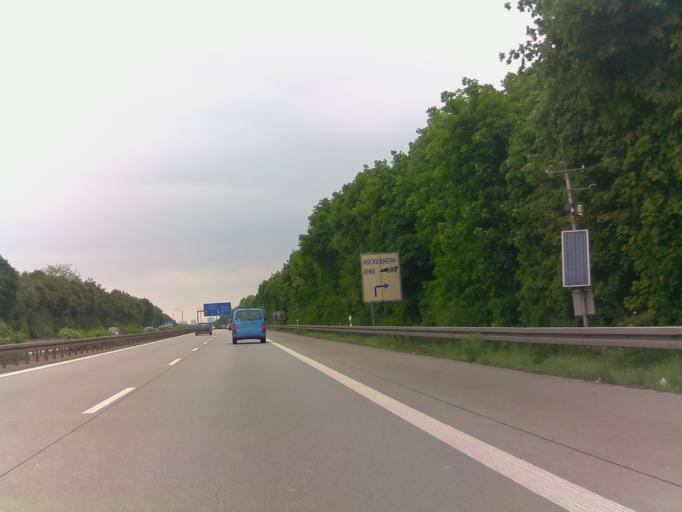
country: DE
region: Baden-Wuerttemberg
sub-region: Karlsruhe Region
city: Hockenheim
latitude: 49.3443
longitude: 8.5546
